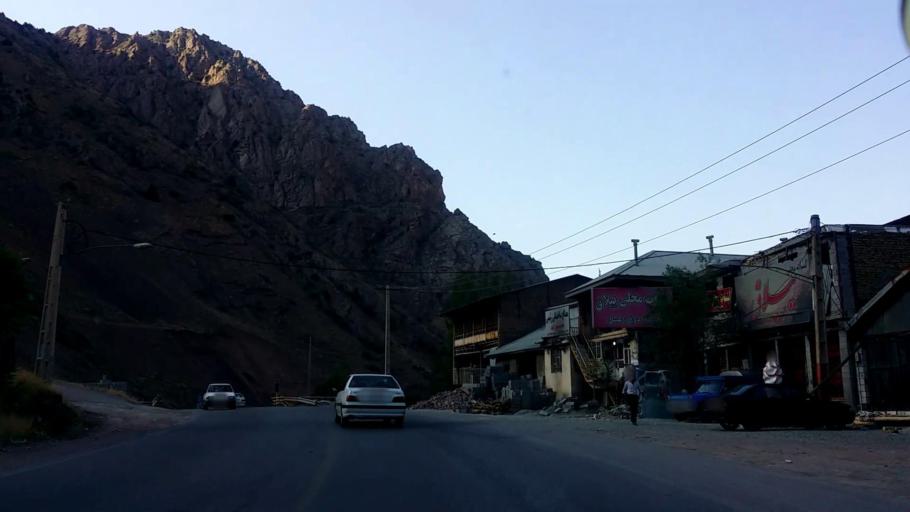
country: IR
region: Tehran
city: Tajrish
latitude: 36.0531
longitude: 51.3139
